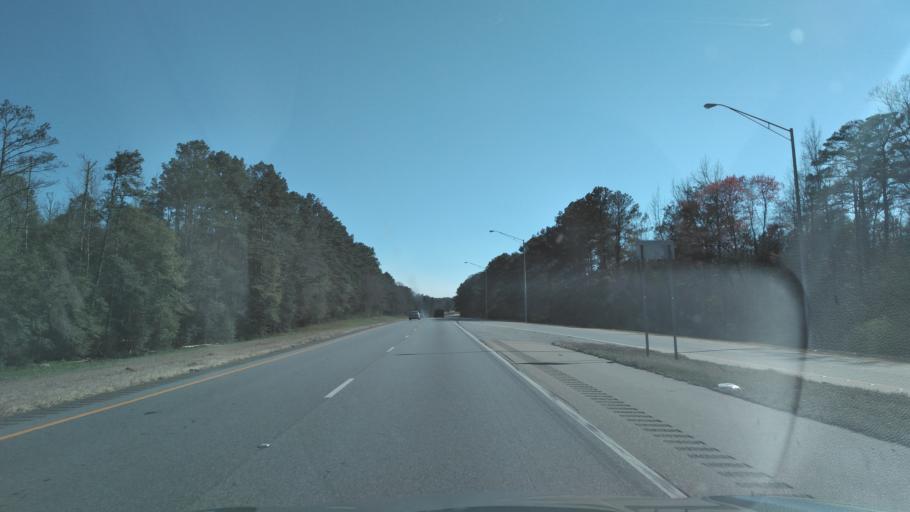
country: US
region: Alabama
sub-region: Butler County
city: Greenville
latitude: 31.8217
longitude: -86.6655
